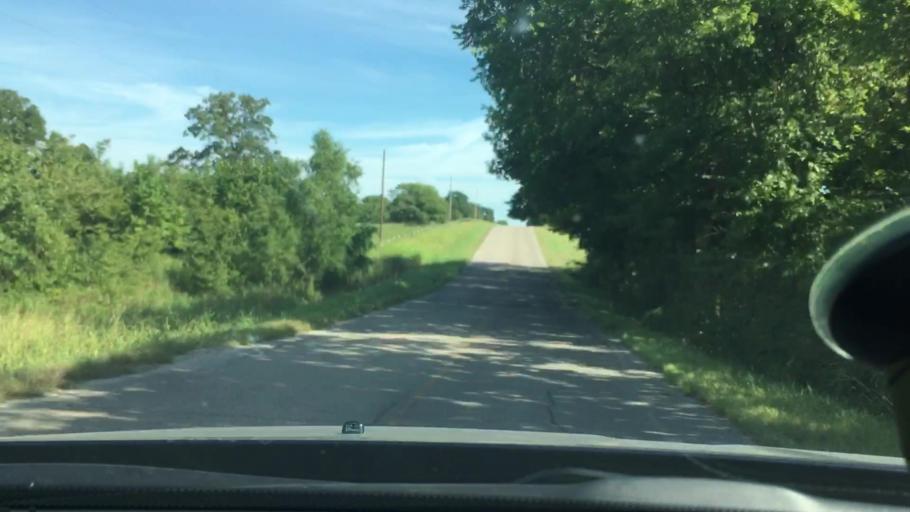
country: US
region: Oklahoma
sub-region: Carter County
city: Lone Grove
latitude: 34.3084
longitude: -97.2824
